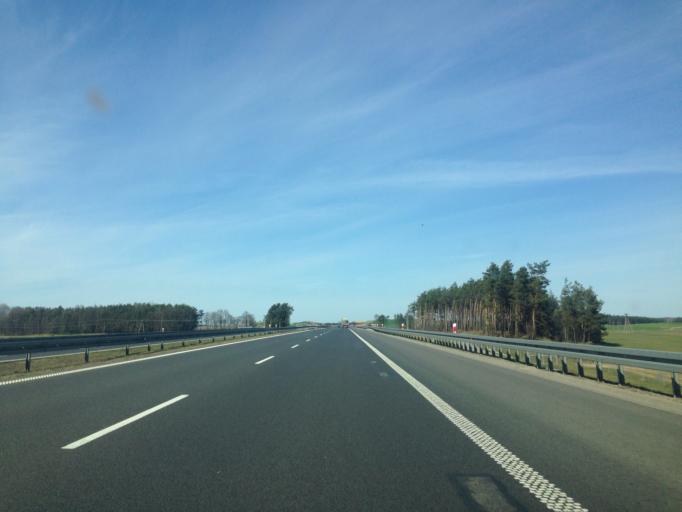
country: PL
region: Pomeranian Voivodeship
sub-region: Powiat starogardzki
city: Smetowo Graniczne
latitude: 53.7838
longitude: 18.6292
